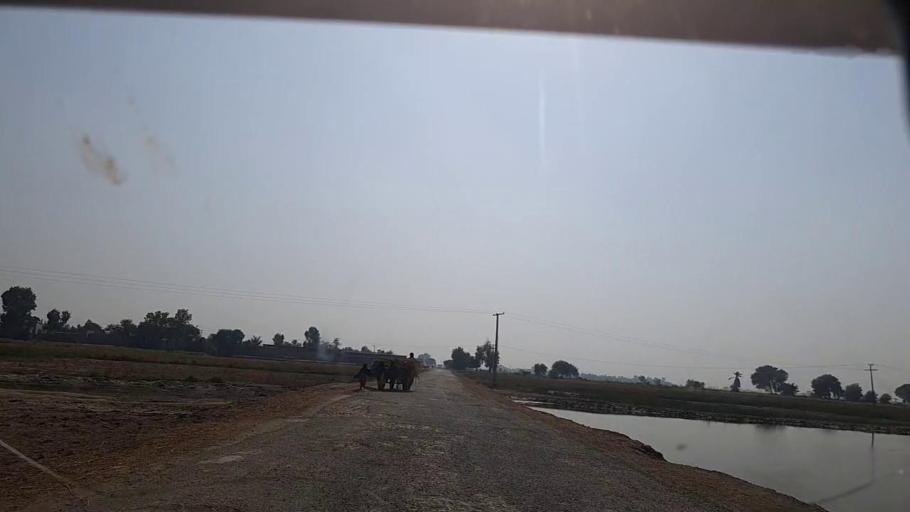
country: PK
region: Sindh
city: Shikarpur
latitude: 28.1005
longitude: 68.6126
